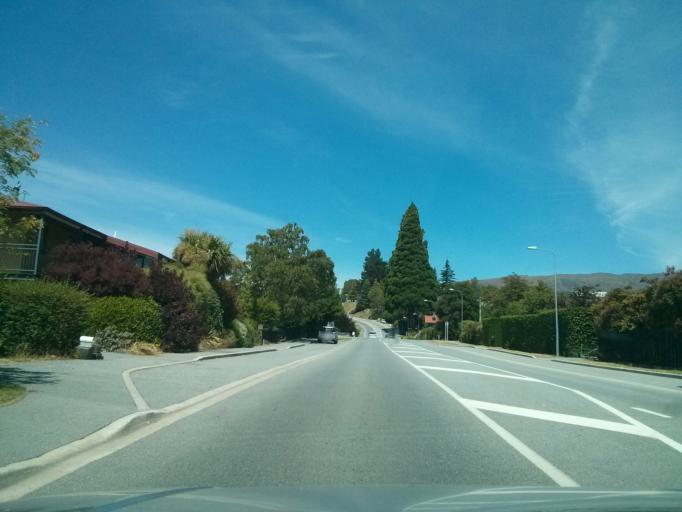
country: NZ
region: Otago
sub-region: Queenstown-Lakes District
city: Wanaka
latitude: -44.7024
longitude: 169.1313
